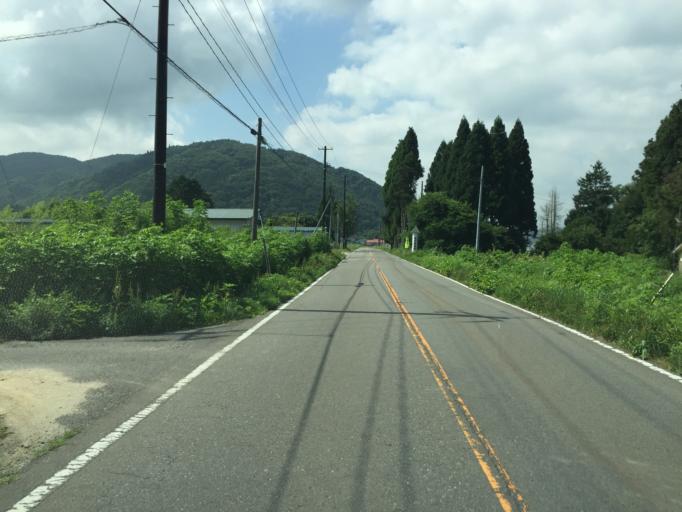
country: JP
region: Fukushima
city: Inawashiro
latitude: 37.4448
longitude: 140.1524
